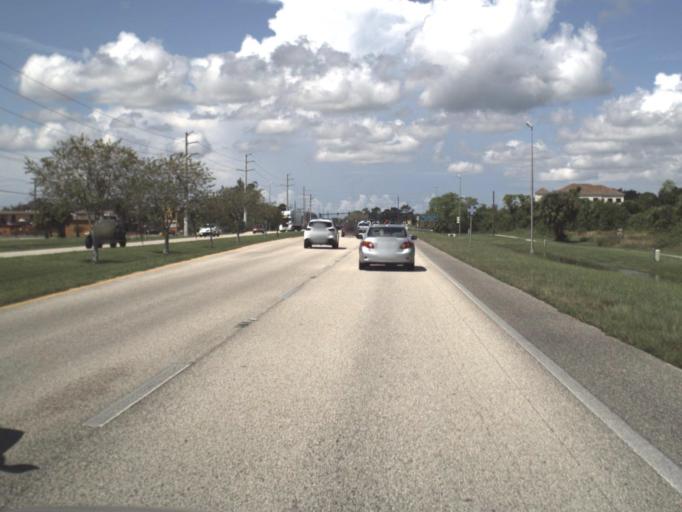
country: US
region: Florida
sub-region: Sarasota County
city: North Port
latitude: 27.0446
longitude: -82.2390
